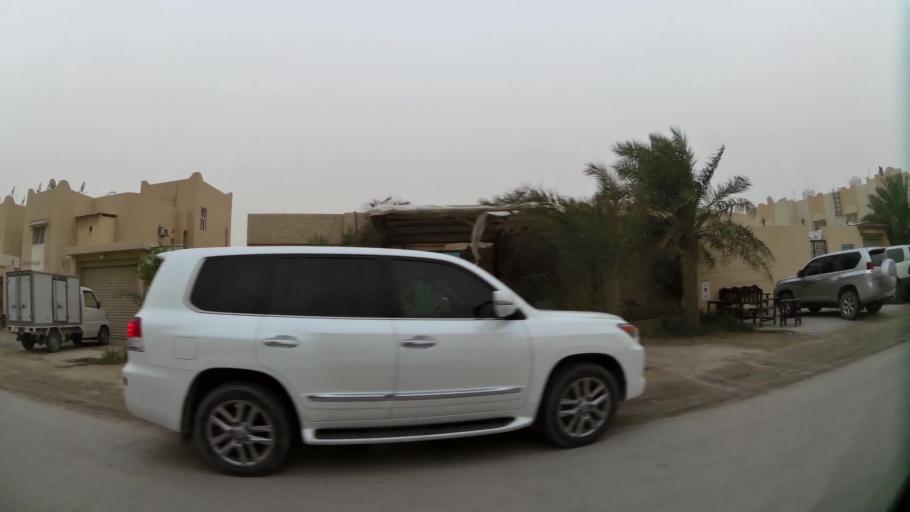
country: QA
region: Baladiyat ad Dawhah
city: Doha
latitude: 25.2323
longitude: 51.4982
